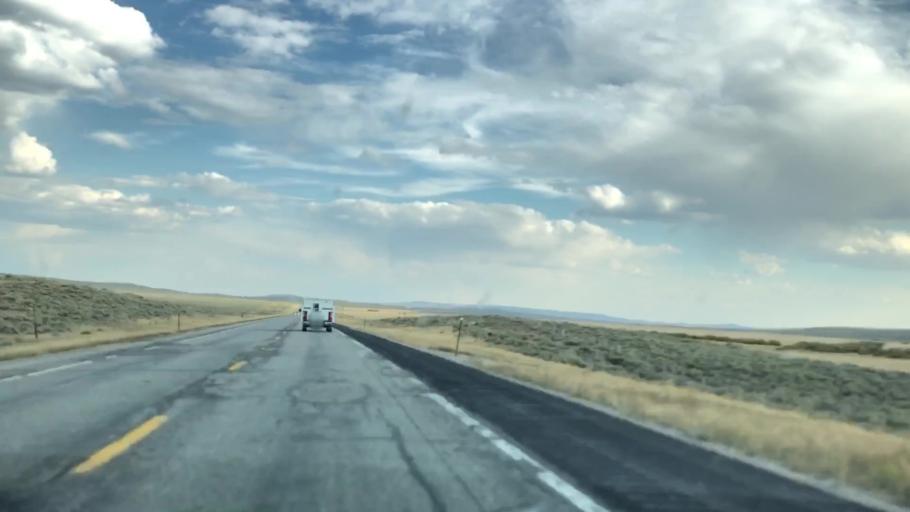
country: US
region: Wyoming
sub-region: Sublette County
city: Pinedale
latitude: 43.0461
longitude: -110.1470
